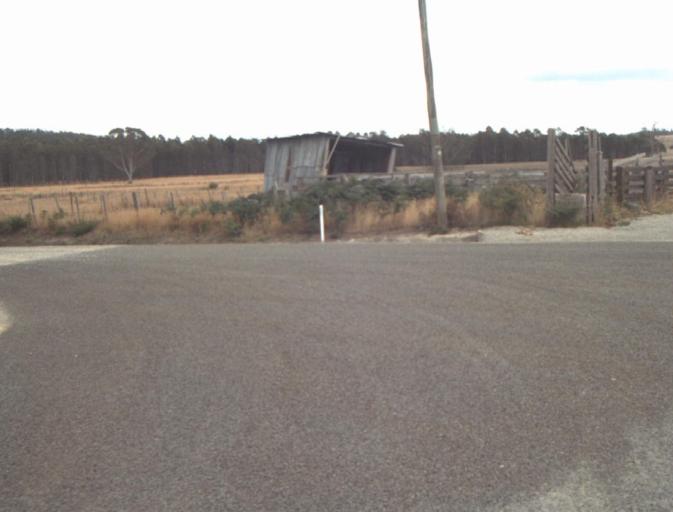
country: AU
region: Tasmania
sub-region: Launceston
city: Mayfield
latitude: -41.2084
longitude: 147.1876
